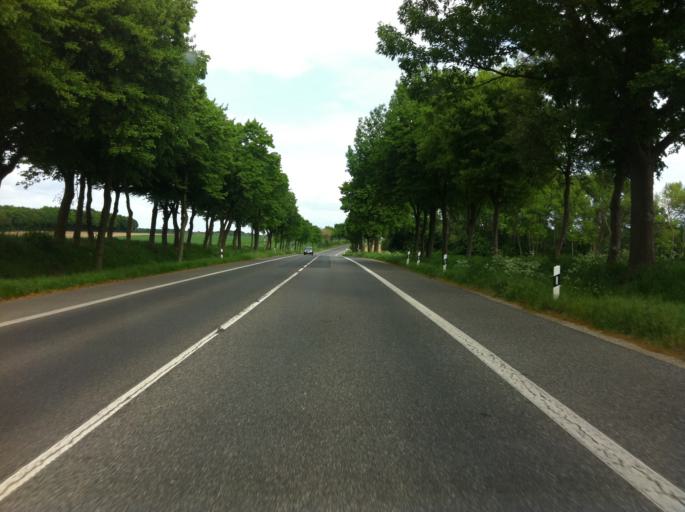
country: DE
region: North Rhine-Westphalia
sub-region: Regierungsbezirk Dusseldorf
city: Niederkruchten
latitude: 51.2131
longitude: 6.2120
